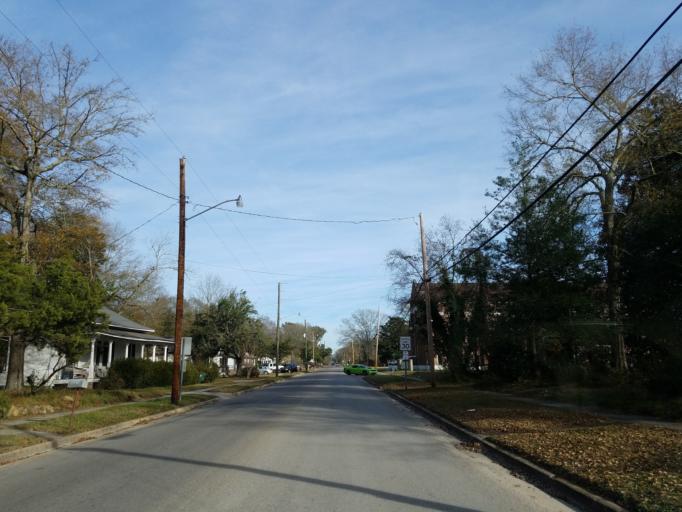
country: US
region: Mississippi
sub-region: Forrest County
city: Hattiesburg
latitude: 31.3320
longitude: -89.3047
